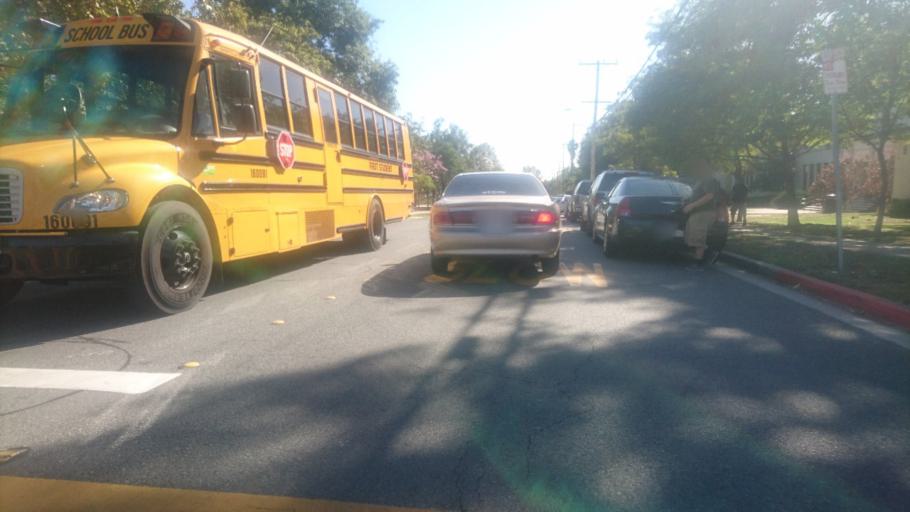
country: US
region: California
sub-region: Los Angeles County
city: East Pasadena
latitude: 34.1422
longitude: -118.0816
